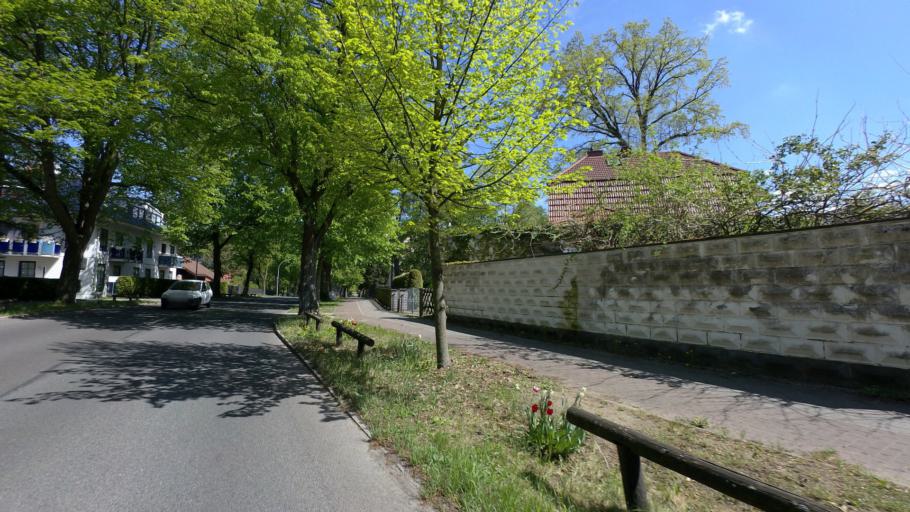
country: DE
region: Berlin
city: Lubars
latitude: 52.6338
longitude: 13.3461
